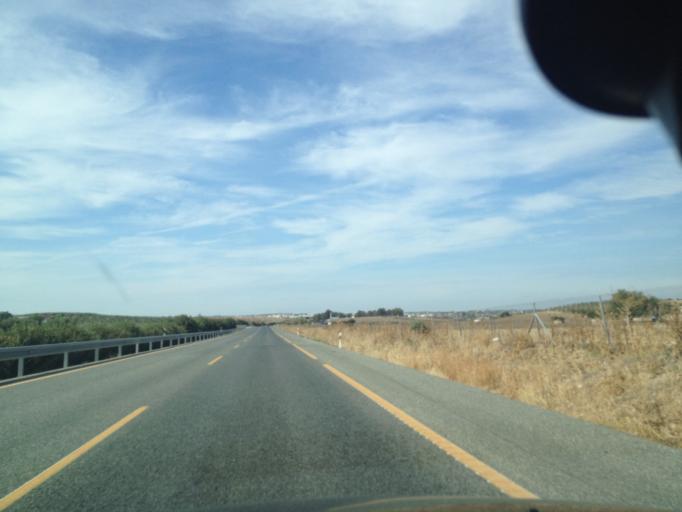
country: ES
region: Andalusia
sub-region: Provincia de Sevilla
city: La Puebla de Cazalla
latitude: 37.2274
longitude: -5.2739
